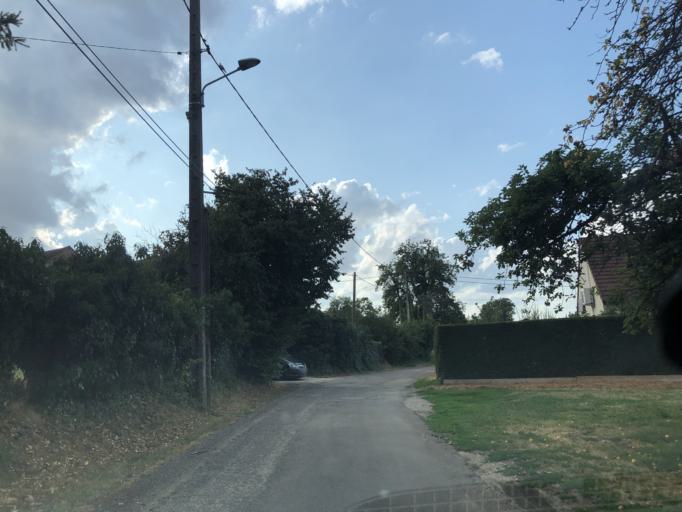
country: FR
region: Bourgogne
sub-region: Departement de l'Yonne
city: Charbuy
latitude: 47.8287
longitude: 3.4514
